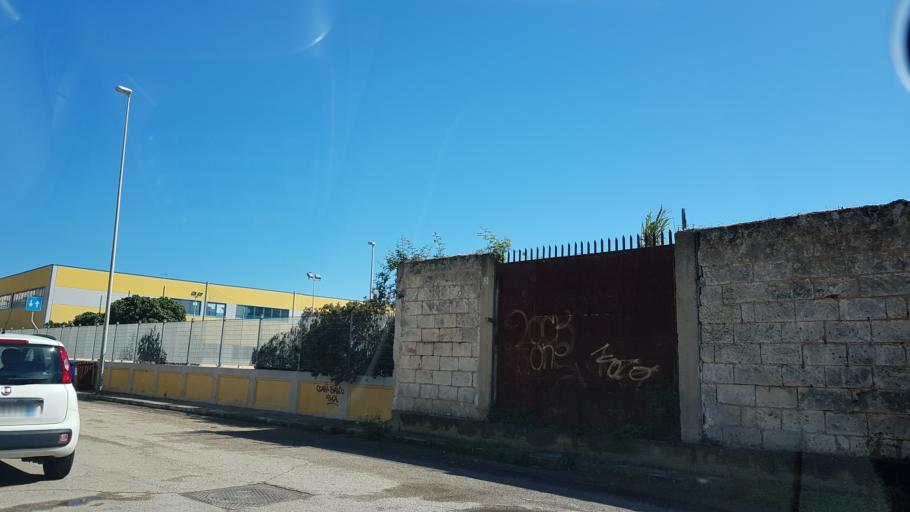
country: IT
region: Apulia
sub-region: Provincia di Brindisi
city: Brindisi
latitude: 40.6354
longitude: 17.9260
